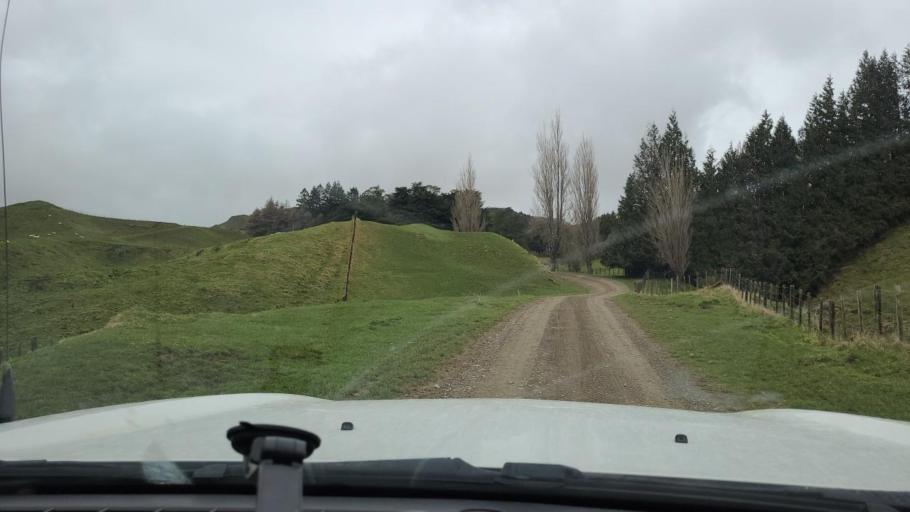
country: NZ
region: Hawke's Bay
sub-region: Wairoa District
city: Wairoa
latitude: -38.5661
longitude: 177.4758
